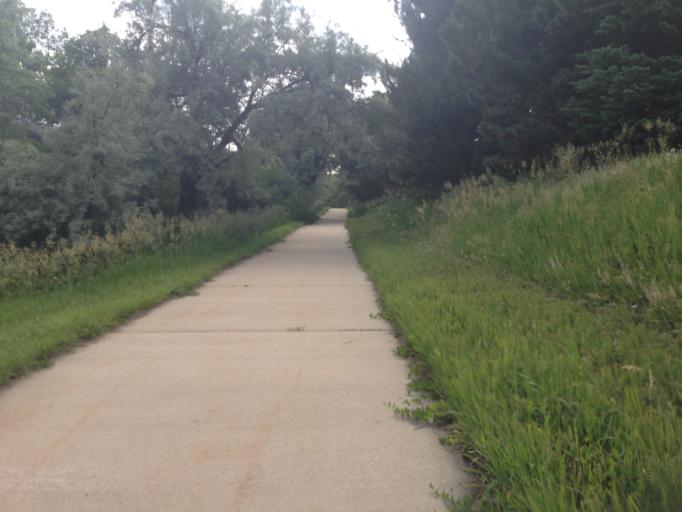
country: US
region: Colorado
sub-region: Boulder County
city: Louisville
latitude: 39.9760
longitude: -105.1457
